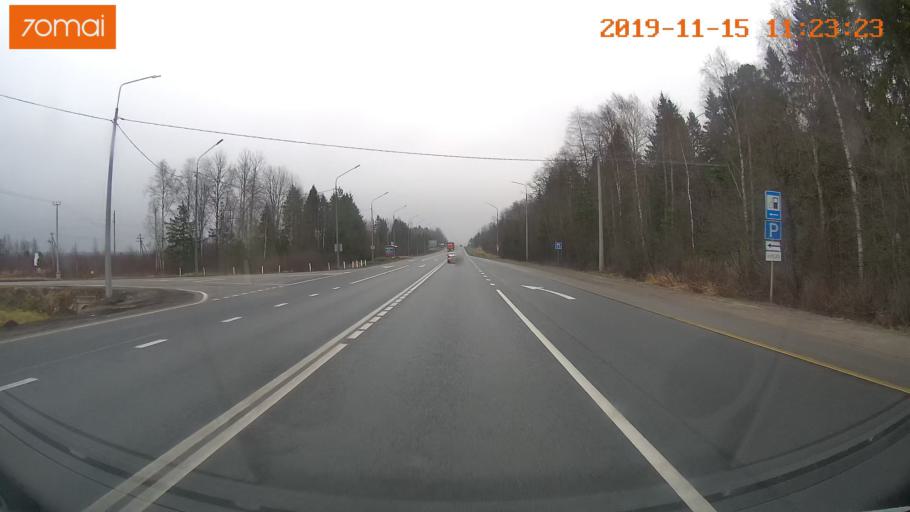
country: RU
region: Vologda
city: Molochnoye
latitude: 59.1511
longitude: 39.3806
